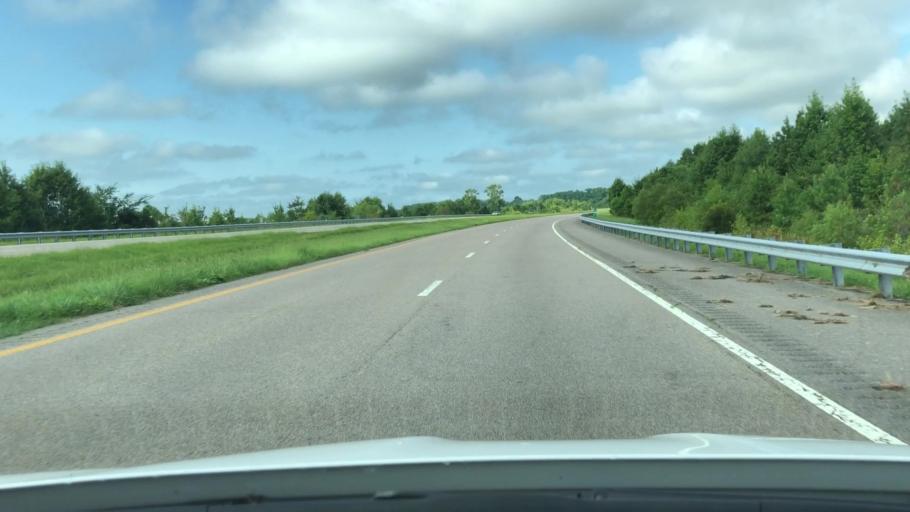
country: US
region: Virginia
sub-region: City of Portsmouth
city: Portsmouth Heights
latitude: 36.6177
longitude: -76.3694
